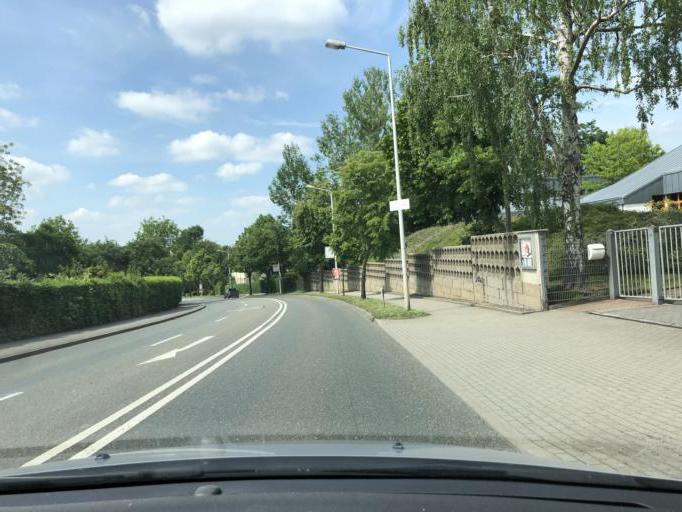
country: DE
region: Thuringia
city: Altenburg
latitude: 50.9894
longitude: 12.4263
